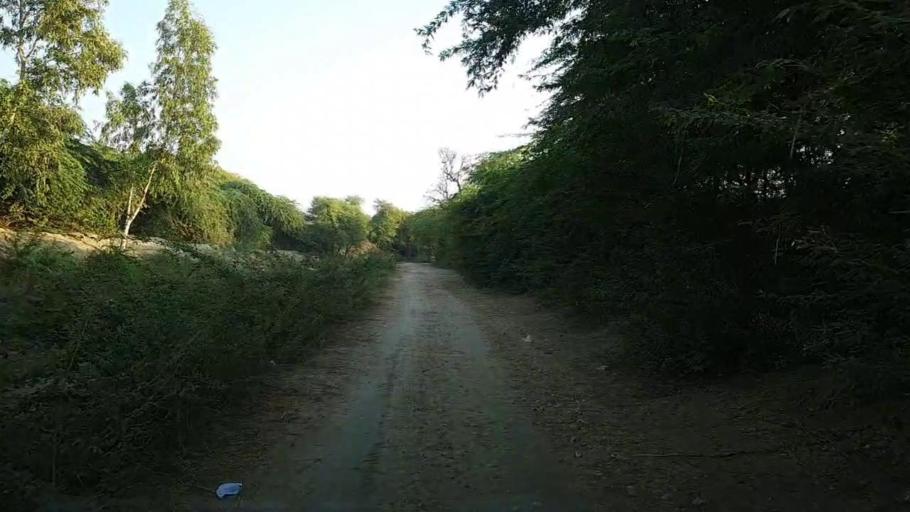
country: PK
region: Sindh
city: Kario
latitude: 24.6969
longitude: 68.6711
